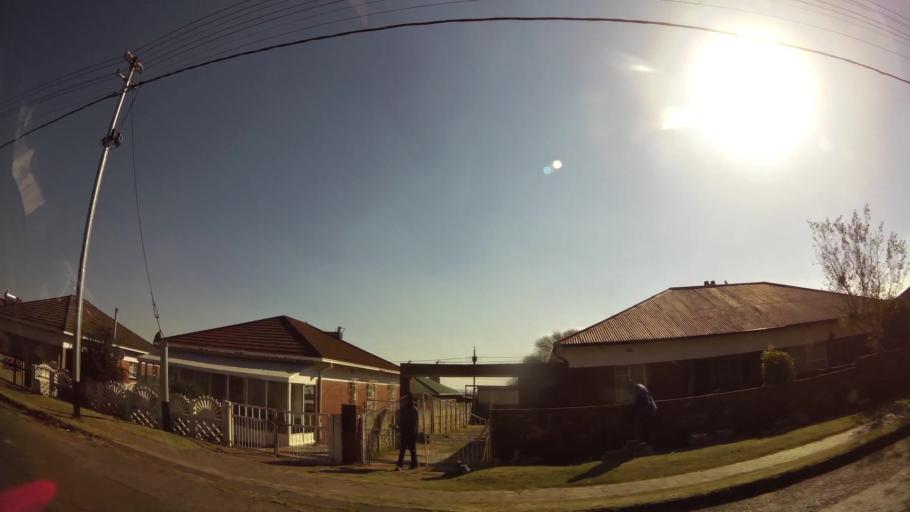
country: ZA
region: Gauteng
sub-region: City of Johannesburg Metropolitan Municipality
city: Johannesburg
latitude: -26.1907
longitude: 27.9784
